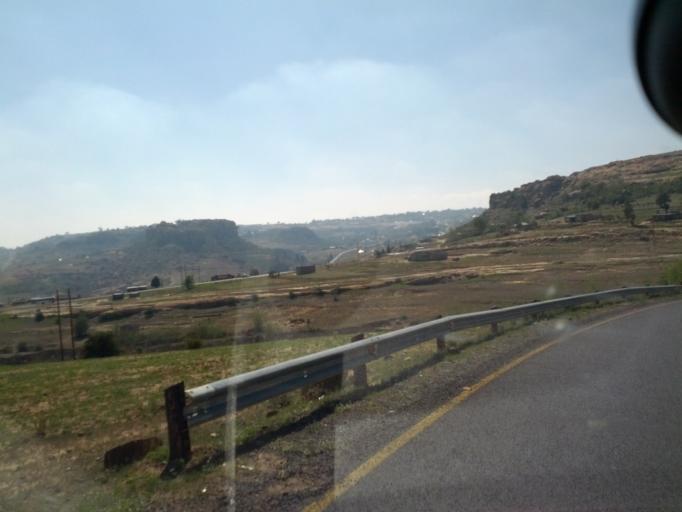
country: LS
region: Berea
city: Teyateyaneng
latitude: -29.1442
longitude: 27.7008
